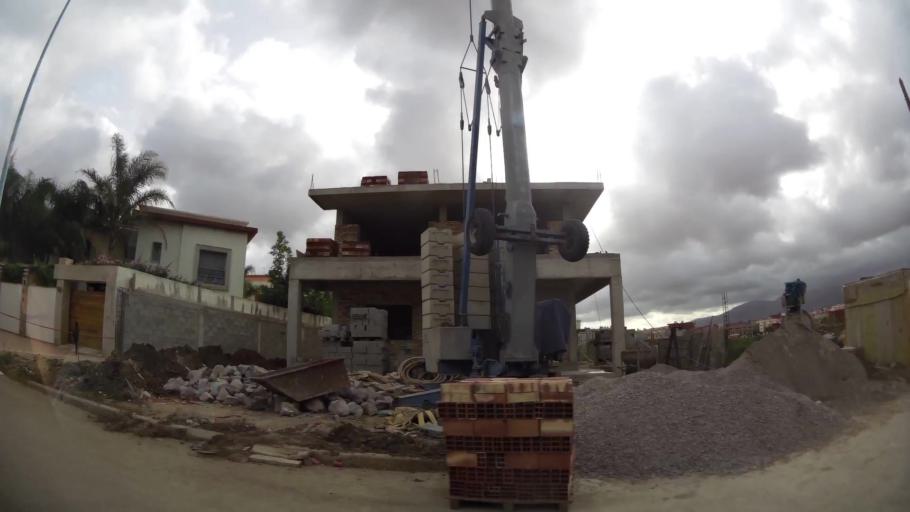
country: MA
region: Oriental
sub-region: Nador
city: Nador
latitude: 35.1633
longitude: -2.9167
